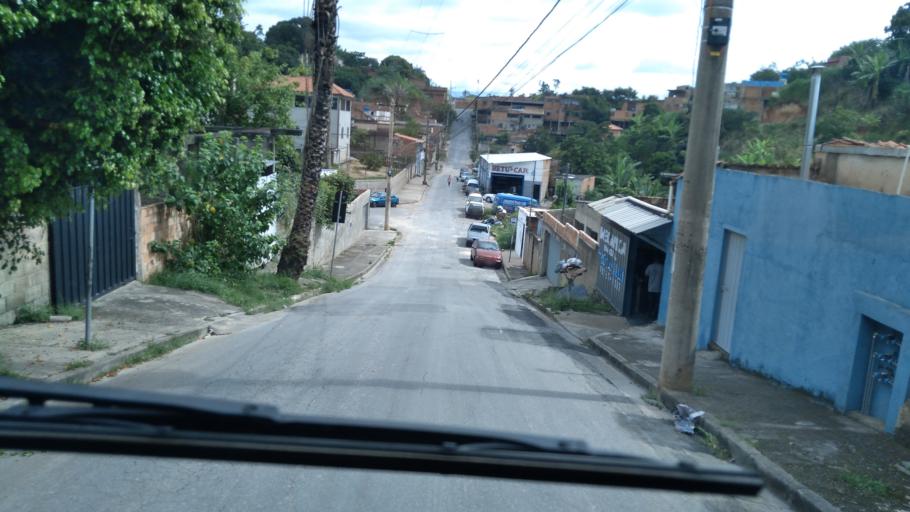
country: BR
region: Minas Gerais
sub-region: Santa Luzia
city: Santa Luzia
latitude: -19.8324
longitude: -43.8949
